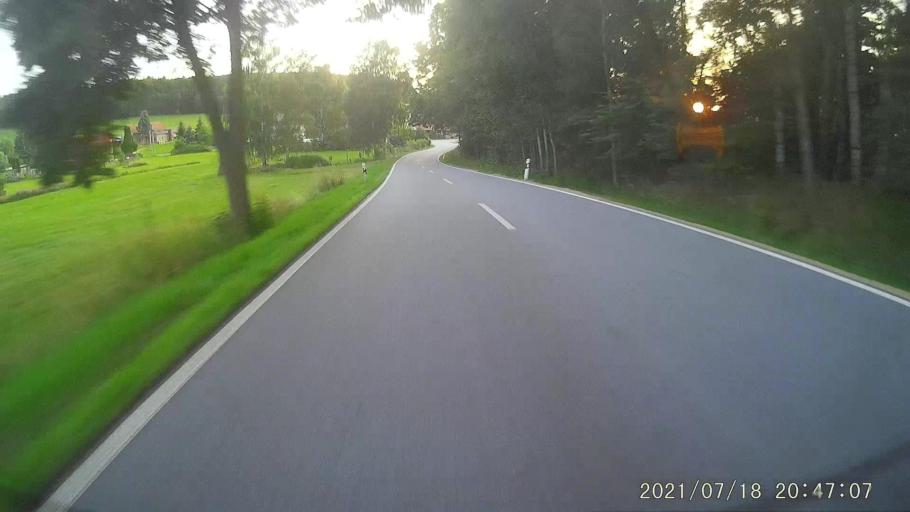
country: DE
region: Saxony
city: Reichenbach
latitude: 51.1869
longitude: 14.7925
